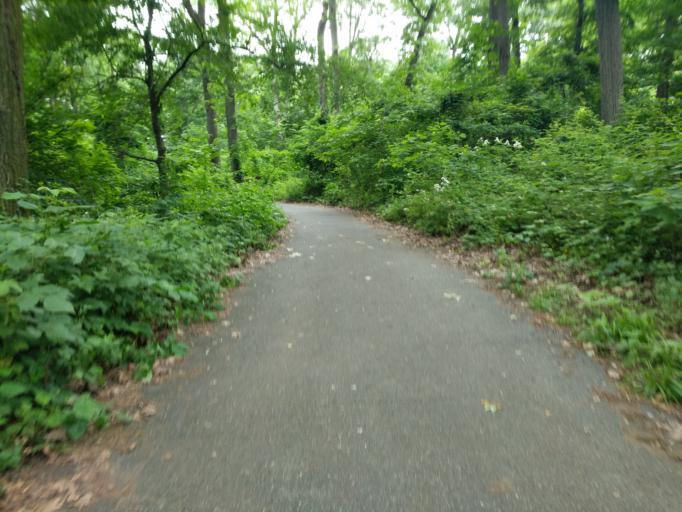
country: US
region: New York
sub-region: Nassau County
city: Bellerose Terrace
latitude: 40.7396
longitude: -73.7414
